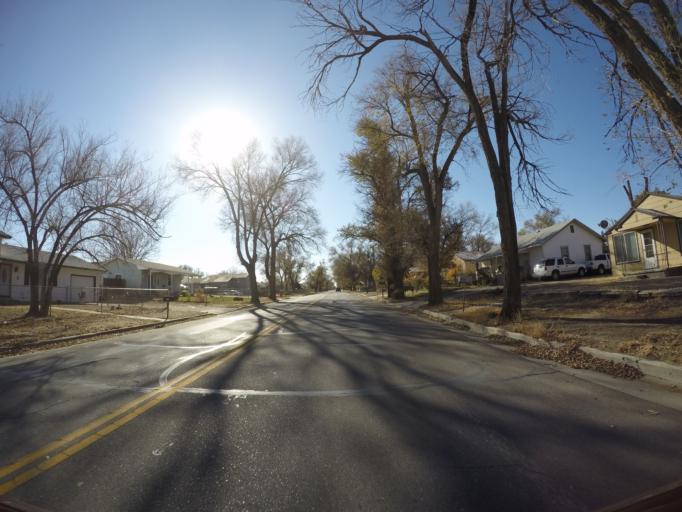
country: US
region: Colorado
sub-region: Otero County
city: La Junta
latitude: 37.9813
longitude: -103.5325
